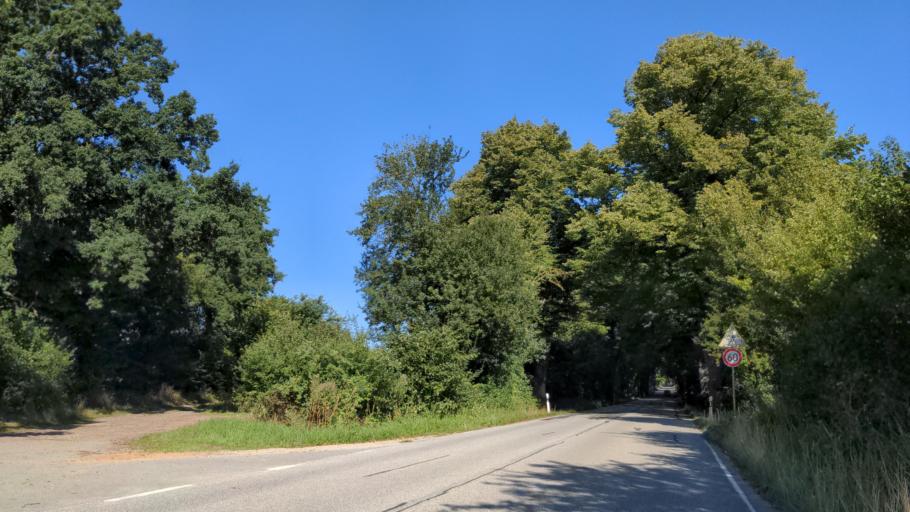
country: DE
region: Mecklenburg-Vorpommern
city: Selmsdorf
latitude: 53.8568
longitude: 10.9171
